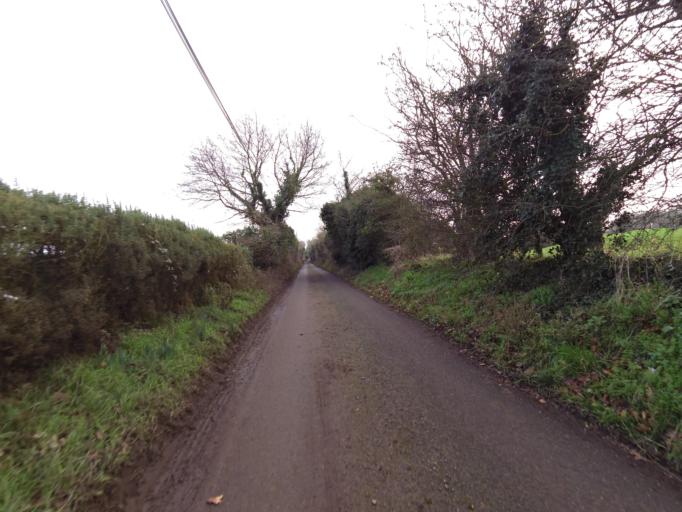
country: GB
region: England
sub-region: Suffolk
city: Woodbridge
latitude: 52.0597
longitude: 1.3156
